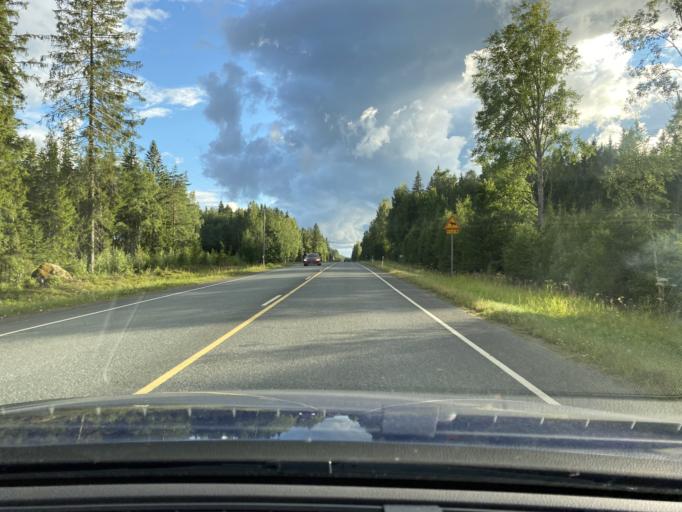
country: FI
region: Haeme
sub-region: Haemeenlinna
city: Renko
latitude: 60.8806
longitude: 24.2350
